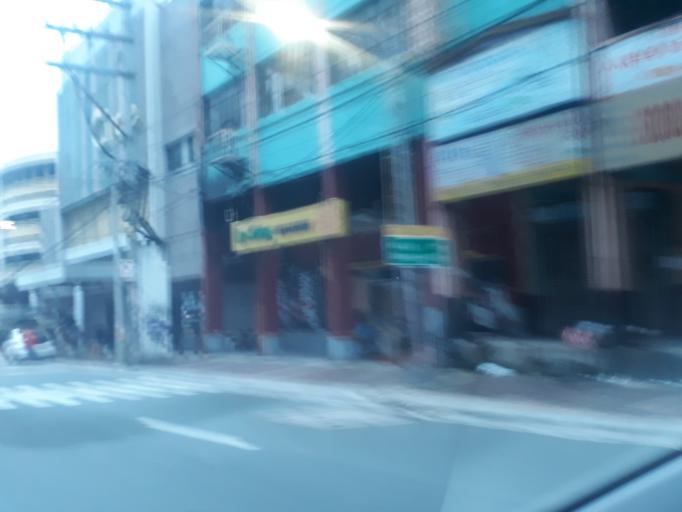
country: PH
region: Calabarzon
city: Del Monte
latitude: 14.6366
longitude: 121.0274
